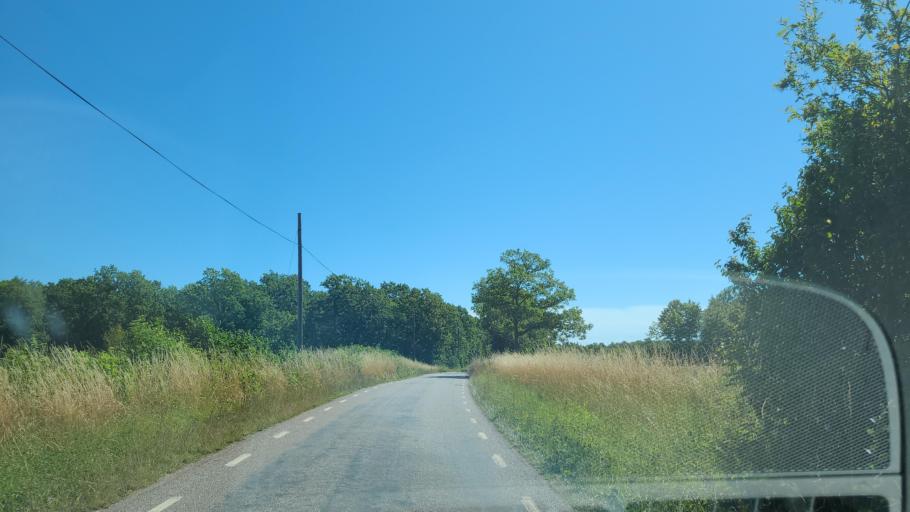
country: SE
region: Kalmar
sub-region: Borgholms Kommun
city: Borgholm
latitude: 56.7615
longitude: 16.6545
